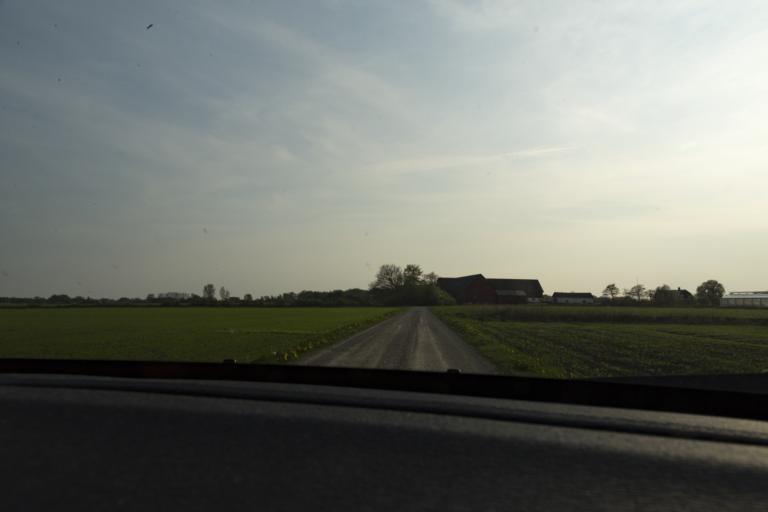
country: SE
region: Halland
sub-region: Varbergs Kommun
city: Varberg
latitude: 57.1591
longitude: 12.2789
